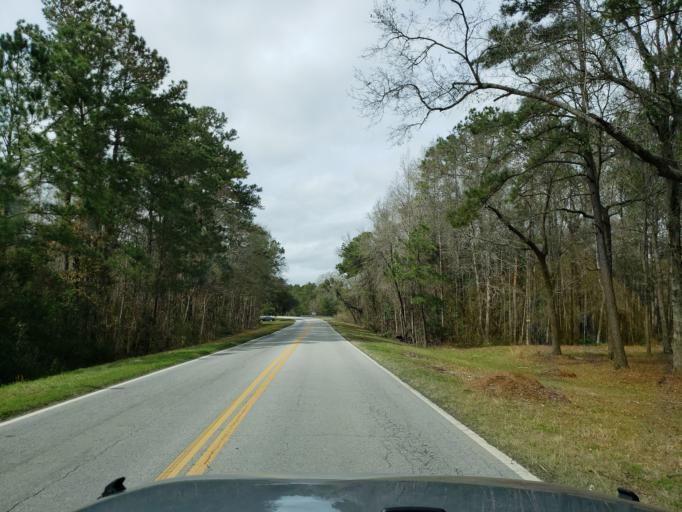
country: US
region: Georgia
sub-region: Chatham County
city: Pooler
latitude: 32.0440
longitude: -81.2803
